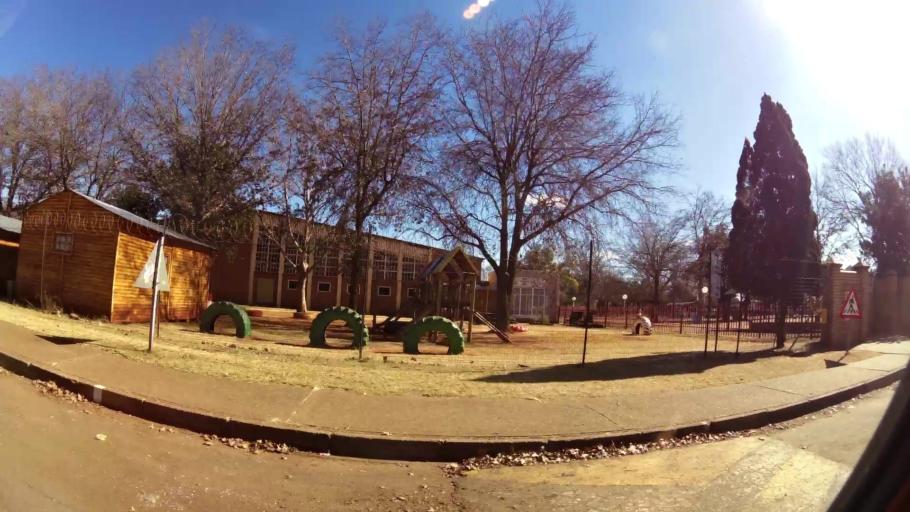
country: ZA
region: Gauteng
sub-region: West Rand District Municipality
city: Carletonville
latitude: -26.3533
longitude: 27.3891
